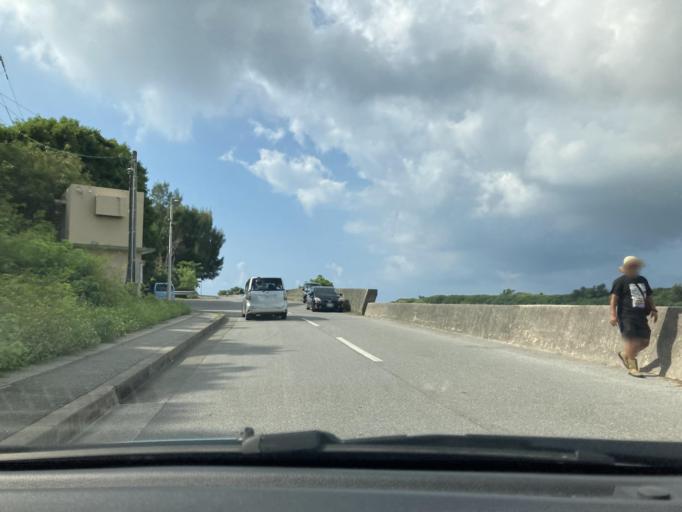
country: JP
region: Okinawa
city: Itoman
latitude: 26.1315
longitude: 127.7711
